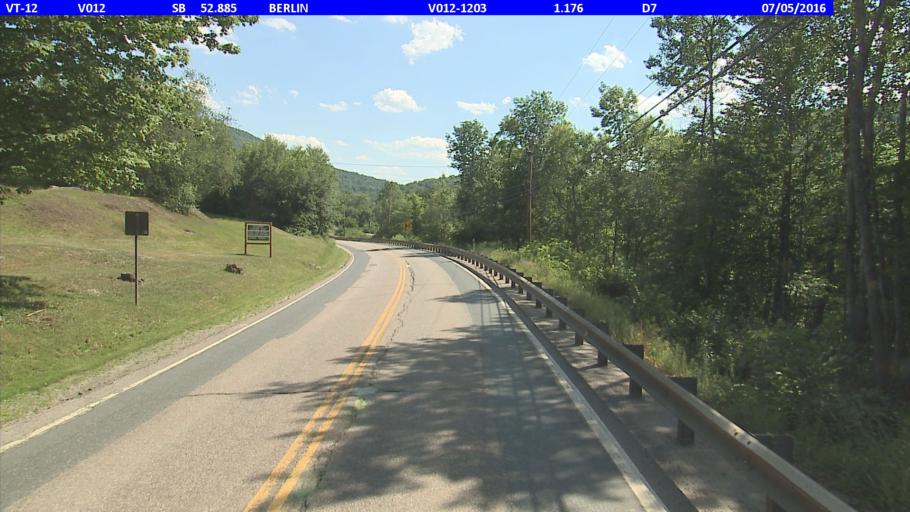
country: US
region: Vermont
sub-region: Washington County
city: Northfield
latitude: 44.1901
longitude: -72.6397
